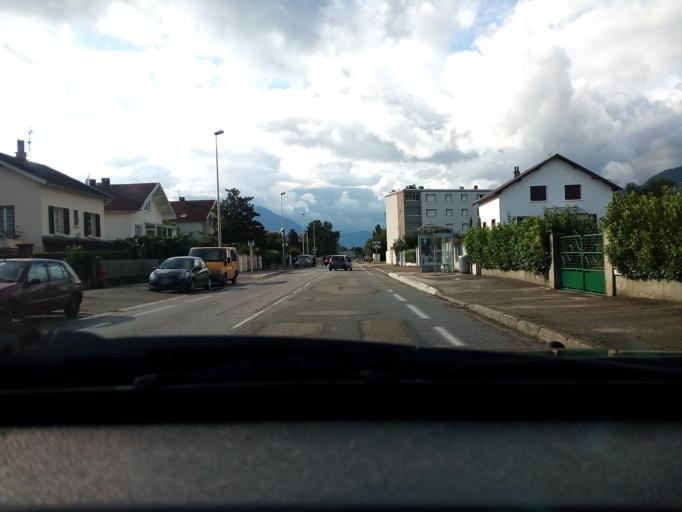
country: FR
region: Rhone-Alpes
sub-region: Departement de l'Isere
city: Poisat
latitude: 45.1596
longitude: 5.7576
